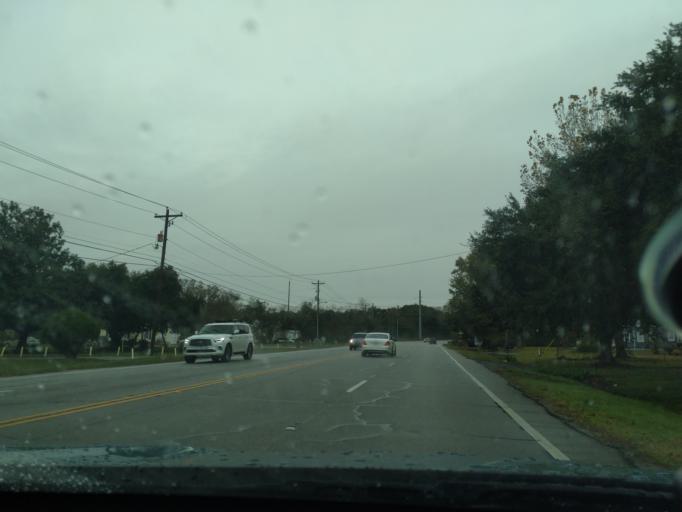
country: US
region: South Carolina
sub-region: Charleston County
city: Folly Beach
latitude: 32.6958
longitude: -79.9662
